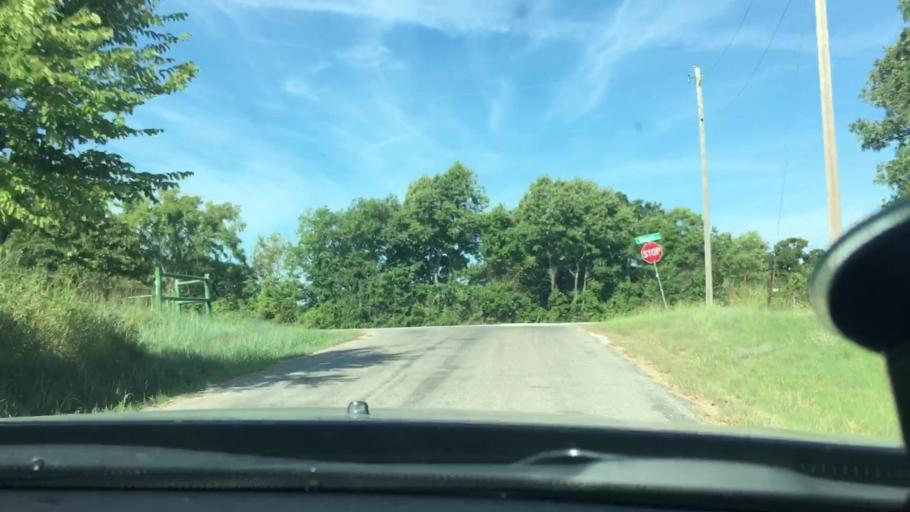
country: US
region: Oklahoma
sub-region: Carter County
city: Lone Grove
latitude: 34.2673
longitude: -97.2819
